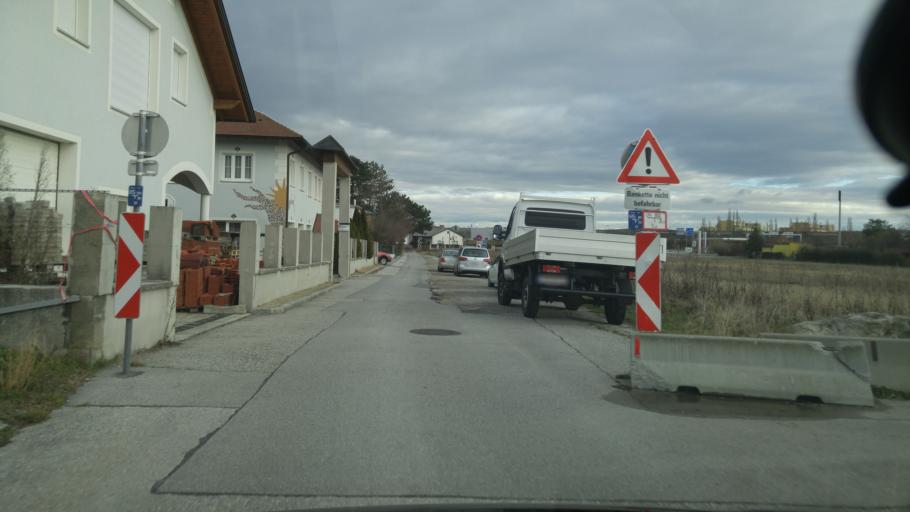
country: AT
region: Lower Austria
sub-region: Politischer Bezirk Baden
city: Bad Voslau
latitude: 47.9565
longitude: 16.2162
